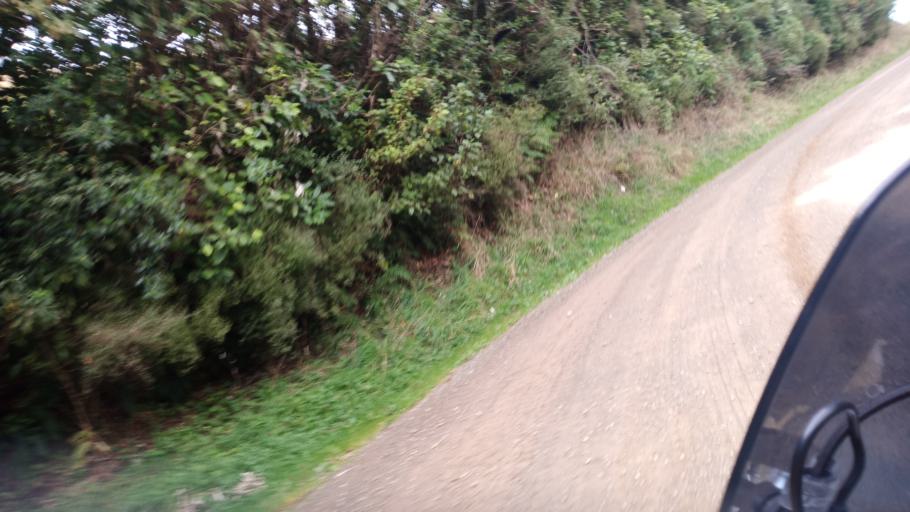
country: NZ
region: Gisborne
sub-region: Gisborne District
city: Gisborne
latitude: -38.4844
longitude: 177.6021
